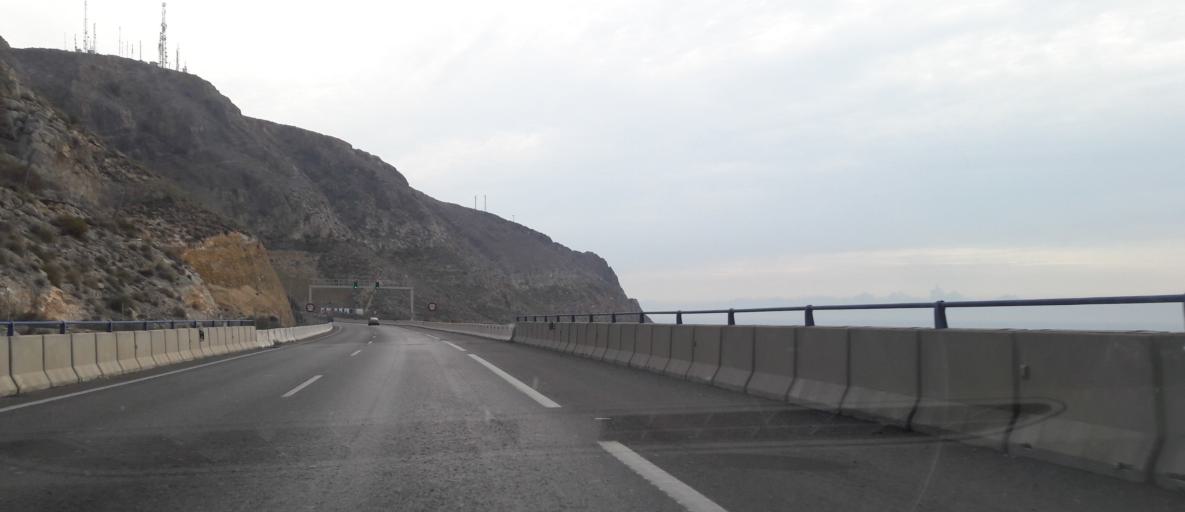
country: ES
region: Andalusia
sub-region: Provincia de Almeria
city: Aguadulce
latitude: 36.8211
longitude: -2.5689
